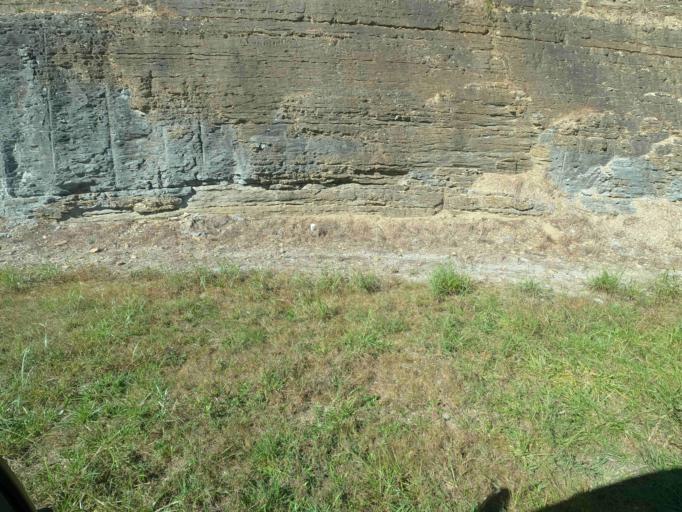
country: US
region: Tennessee
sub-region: Maury County
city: Mount Pleasant
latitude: 35.4785
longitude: -87.2596
